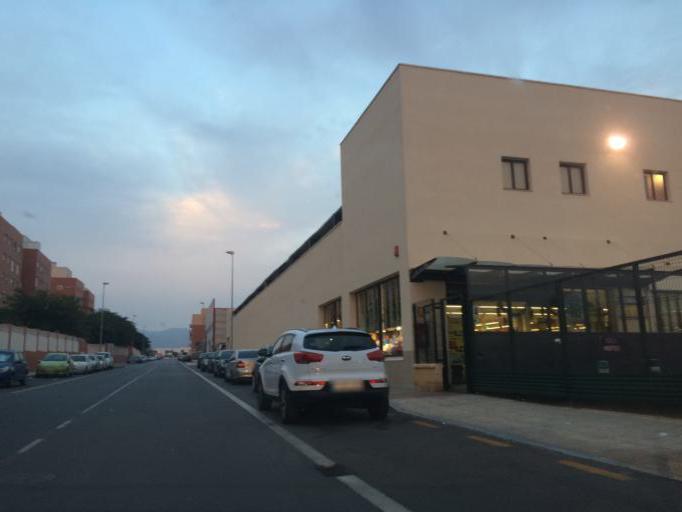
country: ES
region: Andalusia
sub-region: Provincia de Almeria
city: Almeria
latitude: 36.8446
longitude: -2.4363
